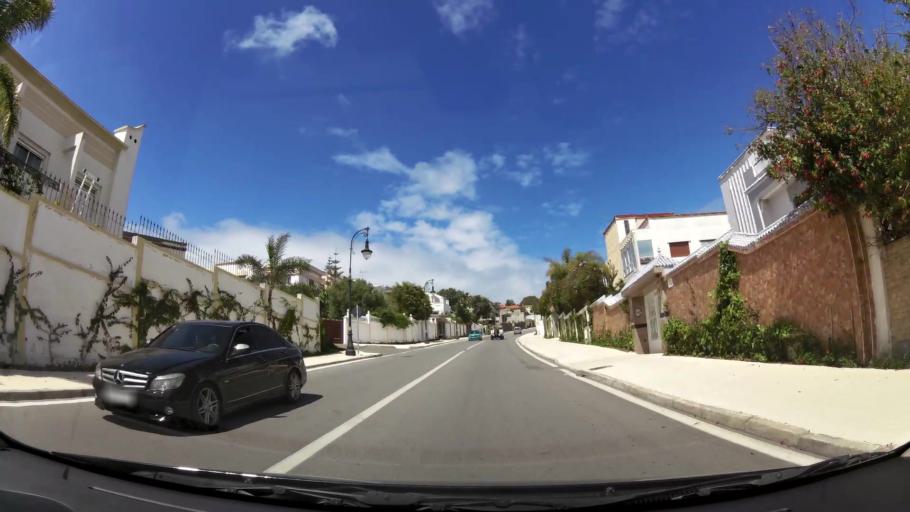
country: MA
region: Tanger-Tetouan
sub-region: Tanger-Assilah
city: Tangier
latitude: 35.7821
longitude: -5.8431
